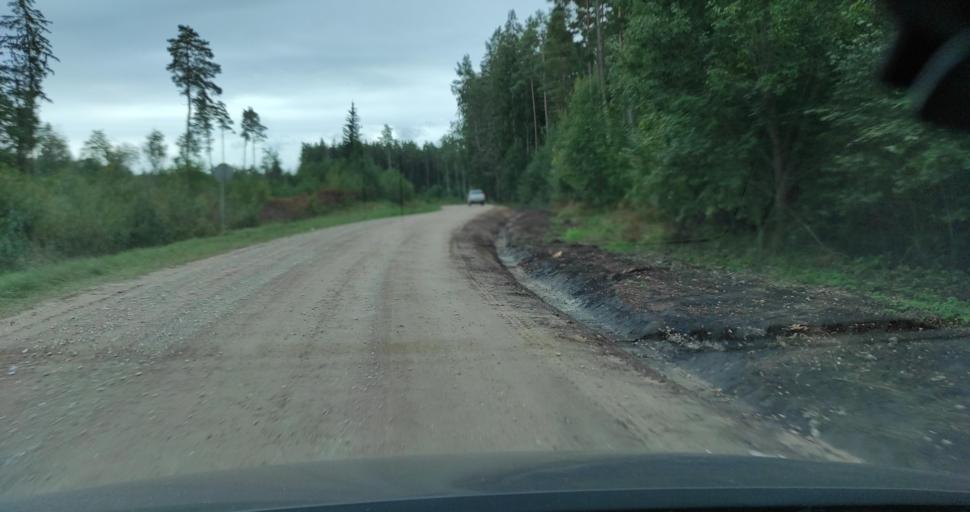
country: LV
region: Talsu Rajons
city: Stende
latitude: 57.0442
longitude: 22.3067
